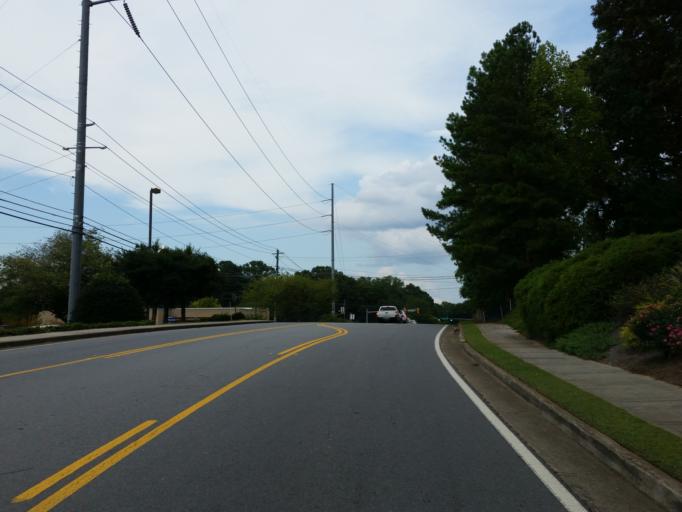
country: US
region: Georgia
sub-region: Cherokee County
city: Woodstock
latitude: 34.0381
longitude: -84.5301
